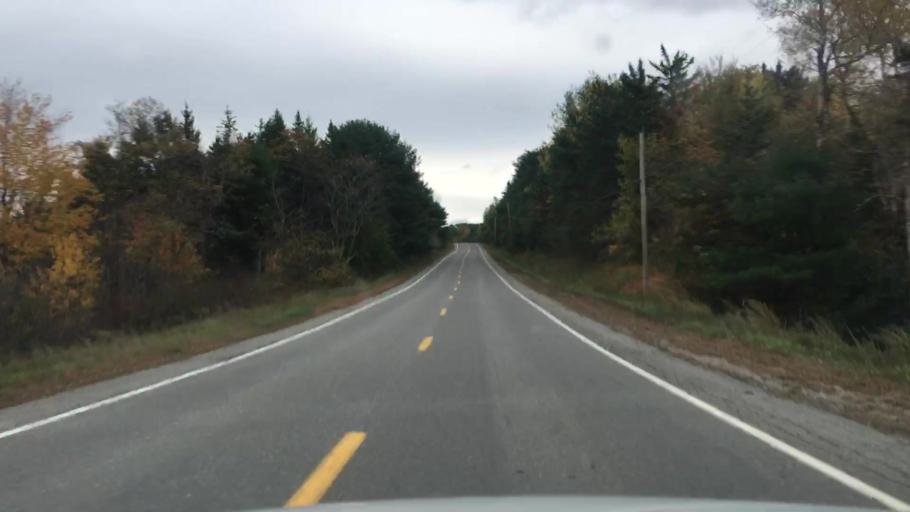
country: US
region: Maine
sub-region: Waldo County
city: Frankfort
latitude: 44.5566
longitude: -68.8566
